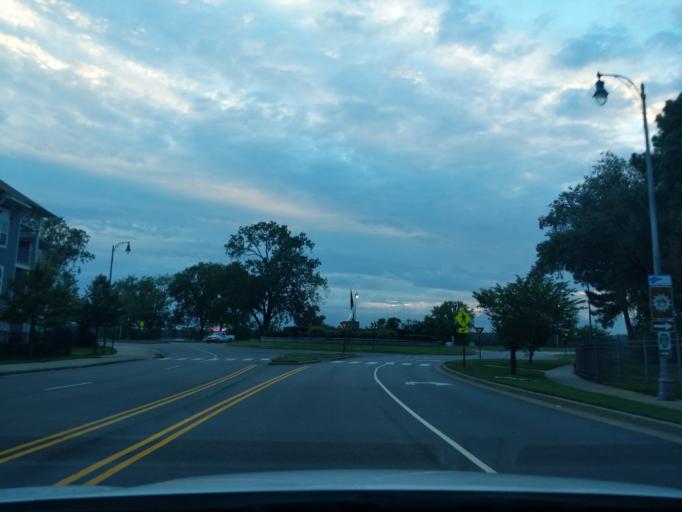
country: US
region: Tennessee
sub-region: Shelby County
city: Memphis
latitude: 35.1591
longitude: -90.0552
